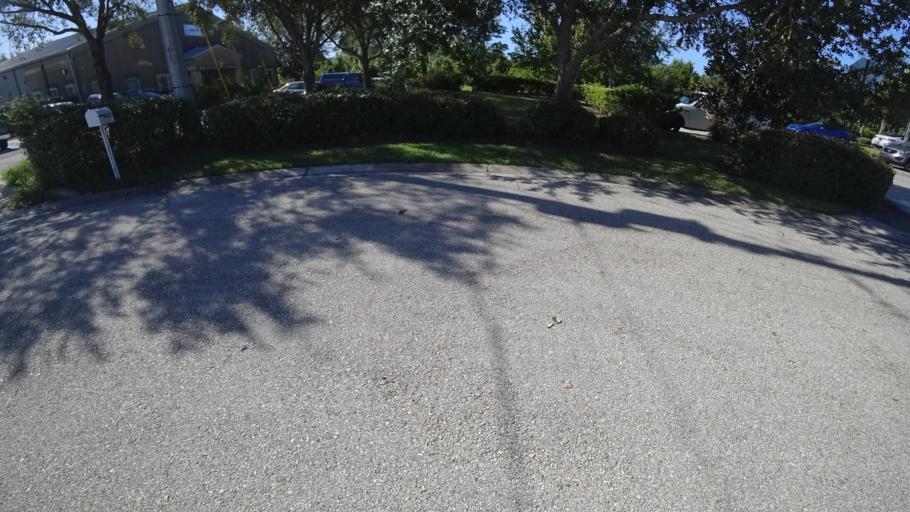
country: US
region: Florida
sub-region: Manatee County
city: Whitfield
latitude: 27.4095
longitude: -82.5375
